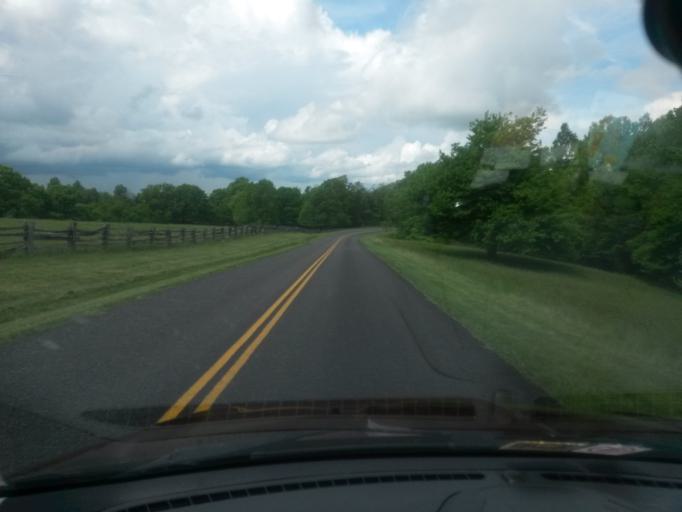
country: US
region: Virginia
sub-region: Floyd County
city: Floyd
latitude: 36.8344
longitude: -80.3273
